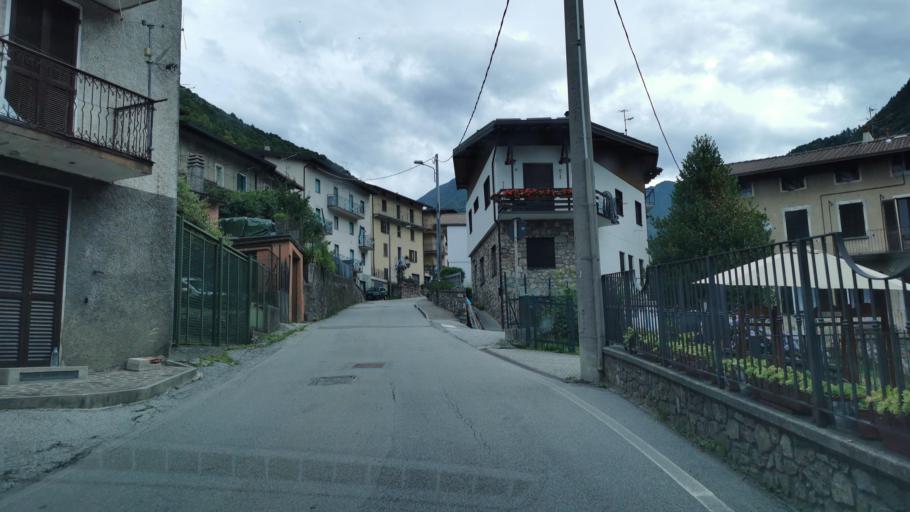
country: IT
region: Lombardy
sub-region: Provincia di Lecco
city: Casargo
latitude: 46.0366
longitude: 9.3855
